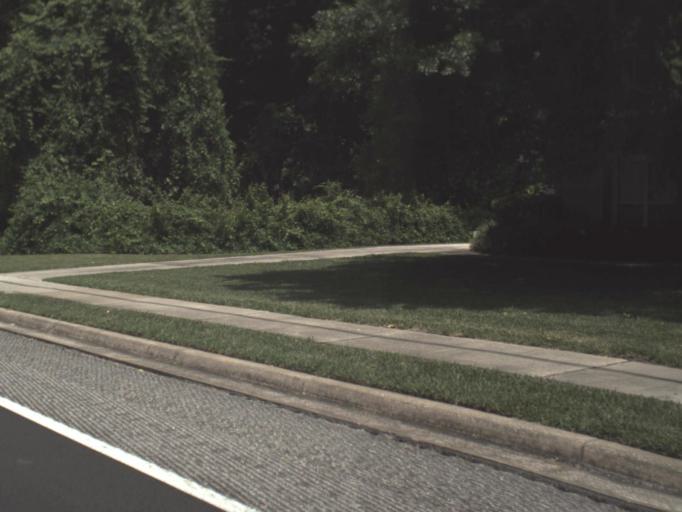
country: US
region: Florida
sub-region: Duval County
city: Jacksonville
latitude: 30.2511
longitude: -81.6385
